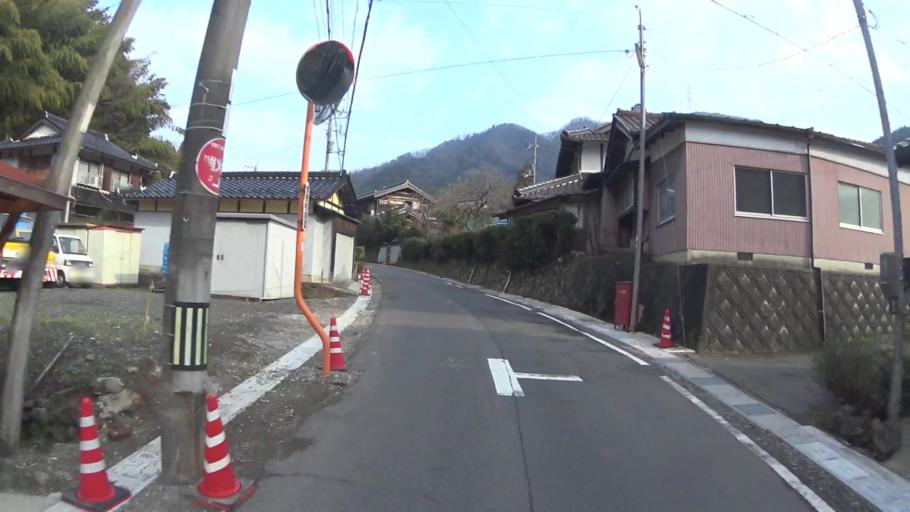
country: JP
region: Kyoto
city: Maizuru
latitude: 35.4087
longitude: 135.3555
